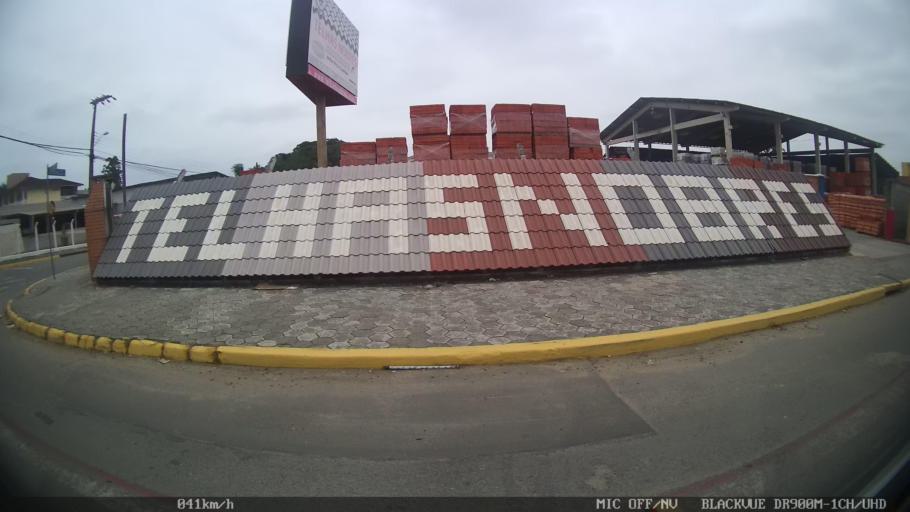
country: BR
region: Santa Catarina
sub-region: Joinville
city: Joinville
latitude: -26.3489
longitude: -48.8470
